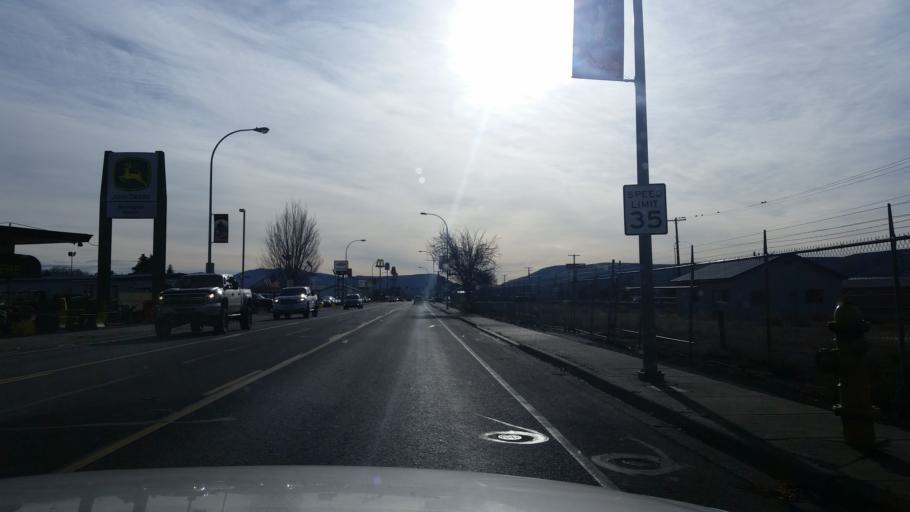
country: US
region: Washington
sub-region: Kittitas County
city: Ellensburg
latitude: 46.9837
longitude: -120.5475
